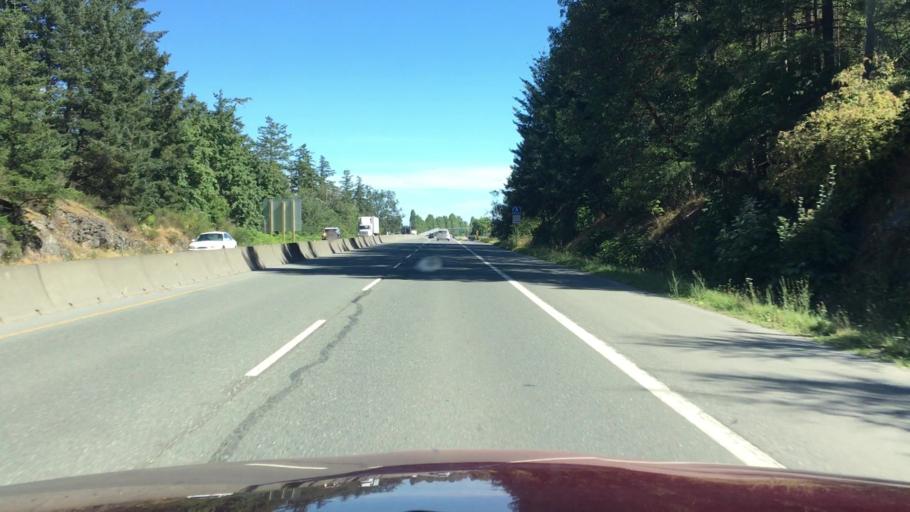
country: CA
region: British Columbia
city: North Saanich
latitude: 48.6675
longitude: -123.4228
